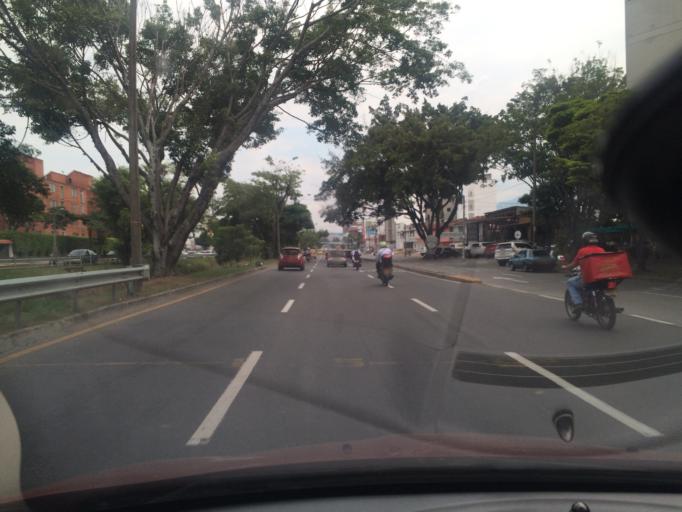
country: CO
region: Valle del Cauca
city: Cali
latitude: 3.4047
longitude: -76.5407
